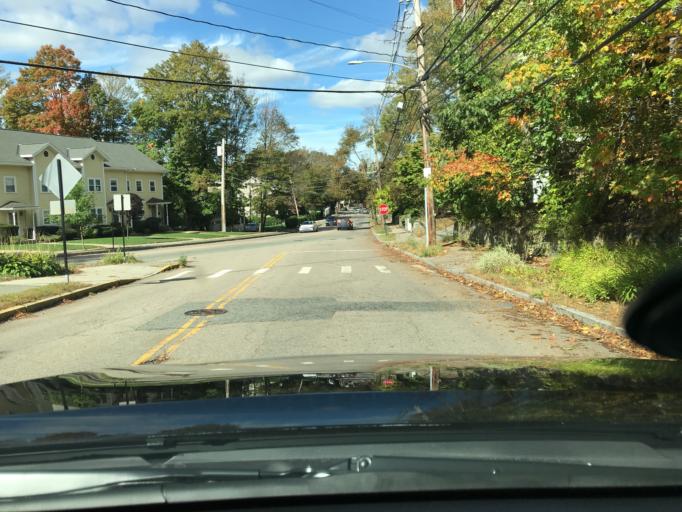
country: US
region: Massachusetts
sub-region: Middlesex County
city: Newton
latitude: 42.3268
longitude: -71.1935
